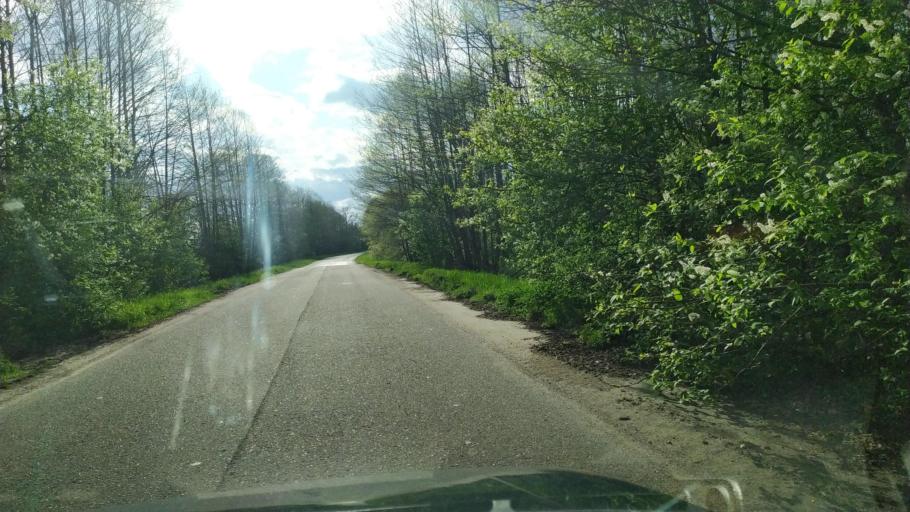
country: BY
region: Brest
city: Pruzhany
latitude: 52.7008
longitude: 24.2048
